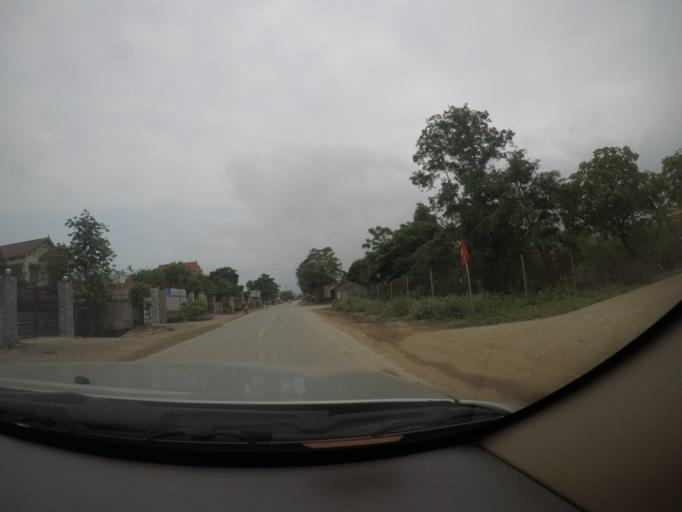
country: VN
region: Quang Binh
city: Kien Giang
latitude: 17.2360
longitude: 106.6939
